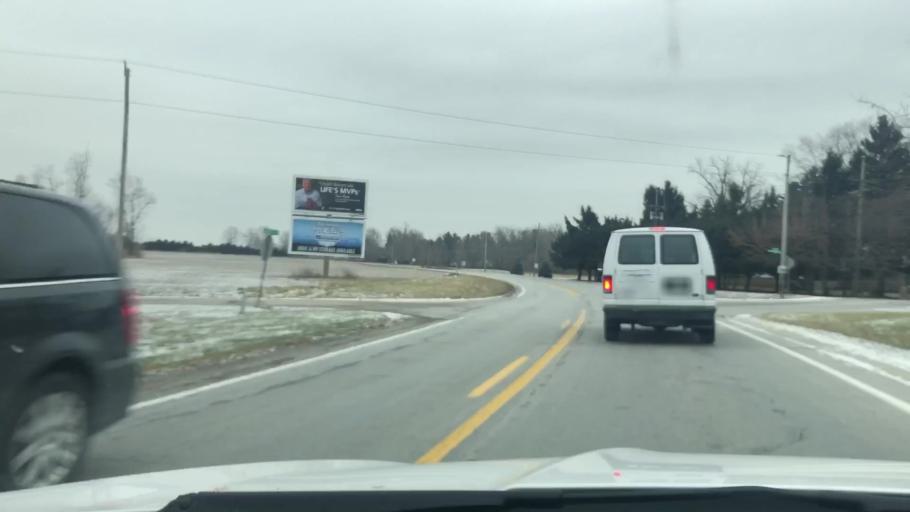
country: US
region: Indiana
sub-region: Fulton County
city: Rochester
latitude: 41.0582
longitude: -86.1691
